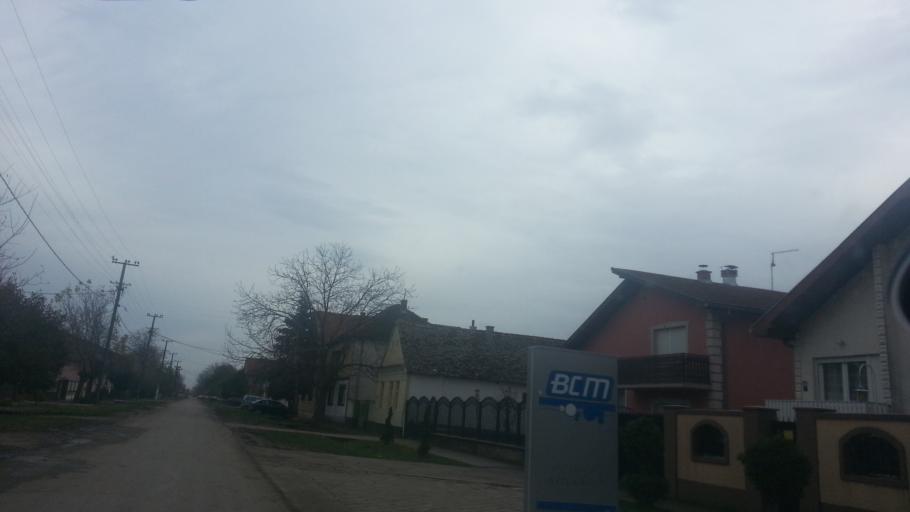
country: RS
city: Golubinci
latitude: 44.9860
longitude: 20.0682
